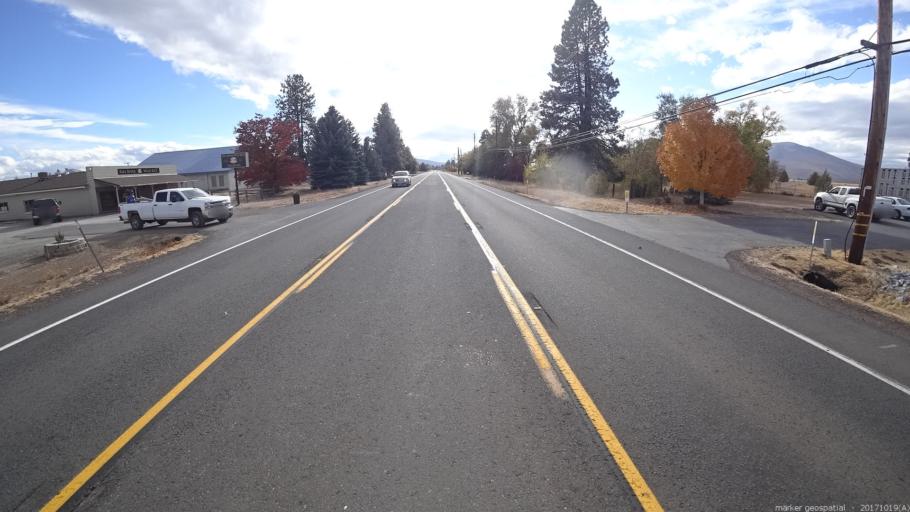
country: US
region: California
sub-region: Shasta County
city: Burney
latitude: 41.0256
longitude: -121.4231
